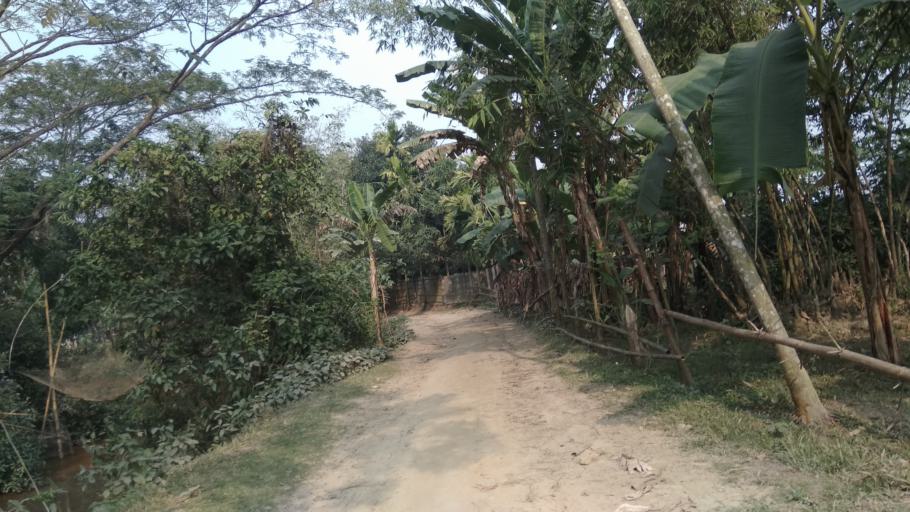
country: BD
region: Dhaka
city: Netrakona
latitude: 24.8913
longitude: 90.6650
